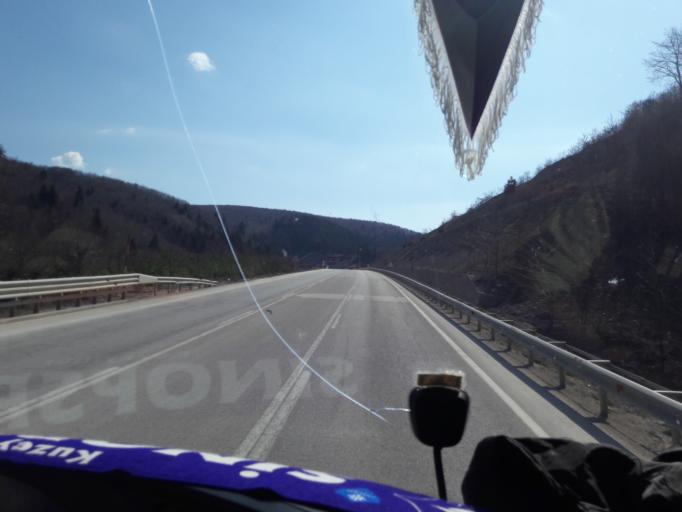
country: TR
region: Sinop
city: Boyabat
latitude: 41.6434
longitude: 34.8974
